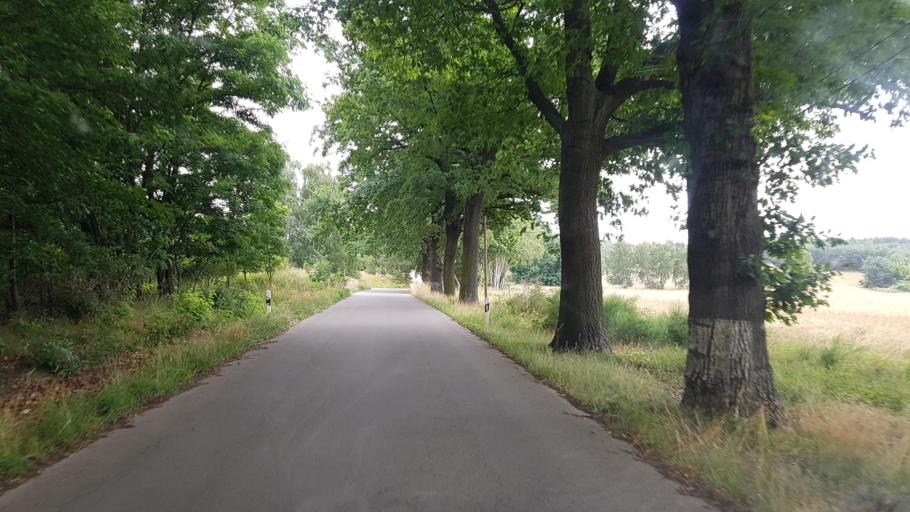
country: DE
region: Brandenburg
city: Altdobern
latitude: 51.6422
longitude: 14.0845
